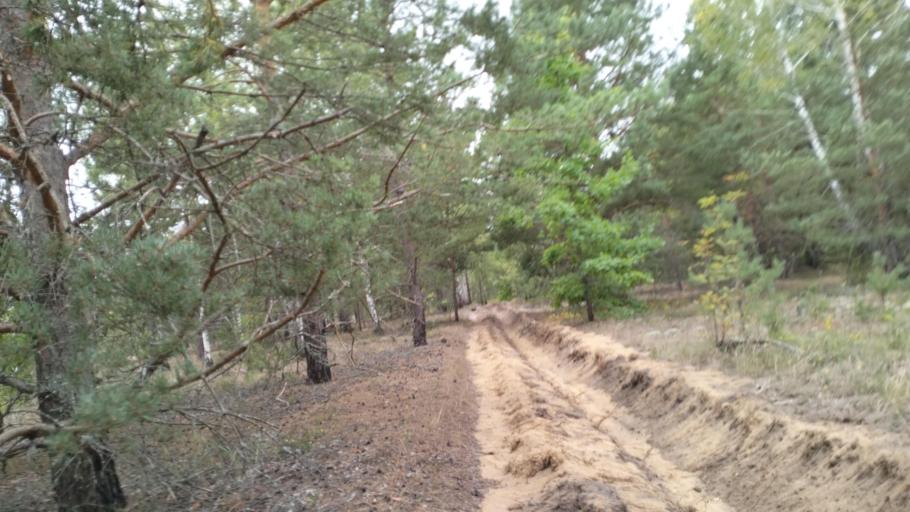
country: BY
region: Brest
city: Davyd-Haradok
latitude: 51.8762
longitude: 27.2108
